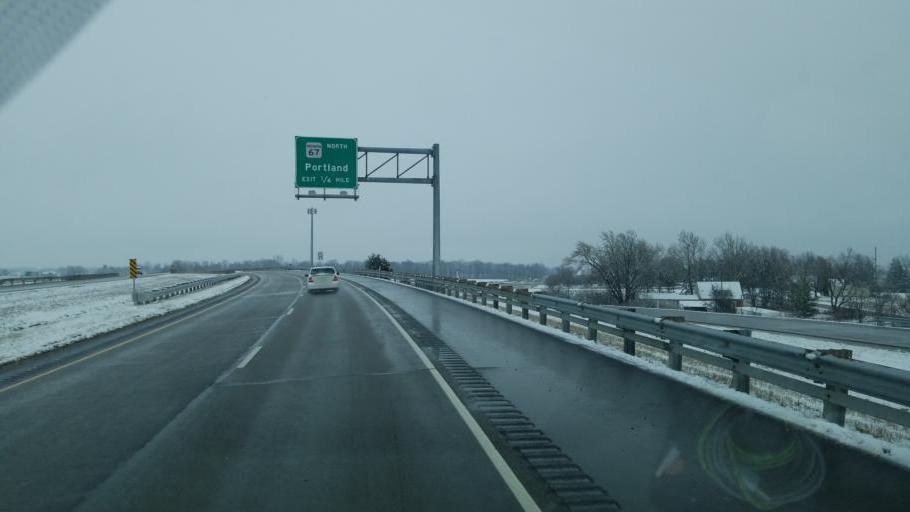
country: US
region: Indiana
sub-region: Delaware County
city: Muncie
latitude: 40.2458
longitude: -85.3672
